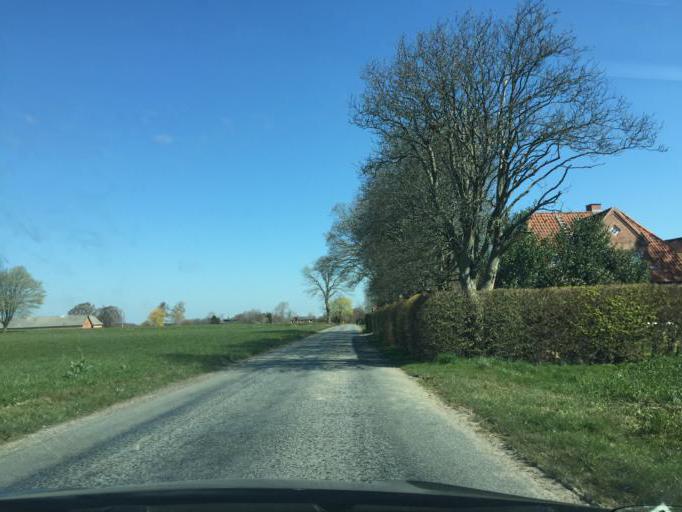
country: DK
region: South Denmark
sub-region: Faaborg-Midtfyn Kommune
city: Ringe
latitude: 55.2569
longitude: 10.5155
